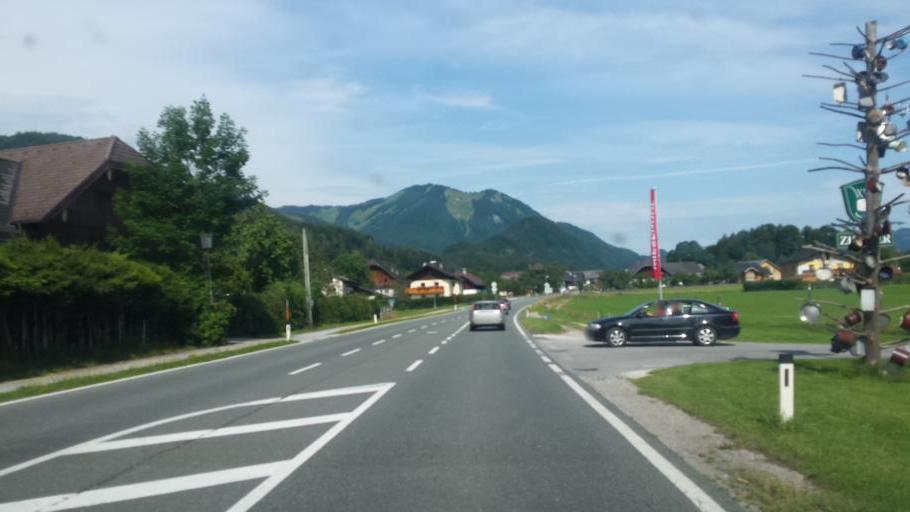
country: AT
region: Upper Austria
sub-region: Politischer Bezirk Gmunden
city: Sankt Wolfgang im Salzkammergut
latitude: 47.7208
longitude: 13.4299
